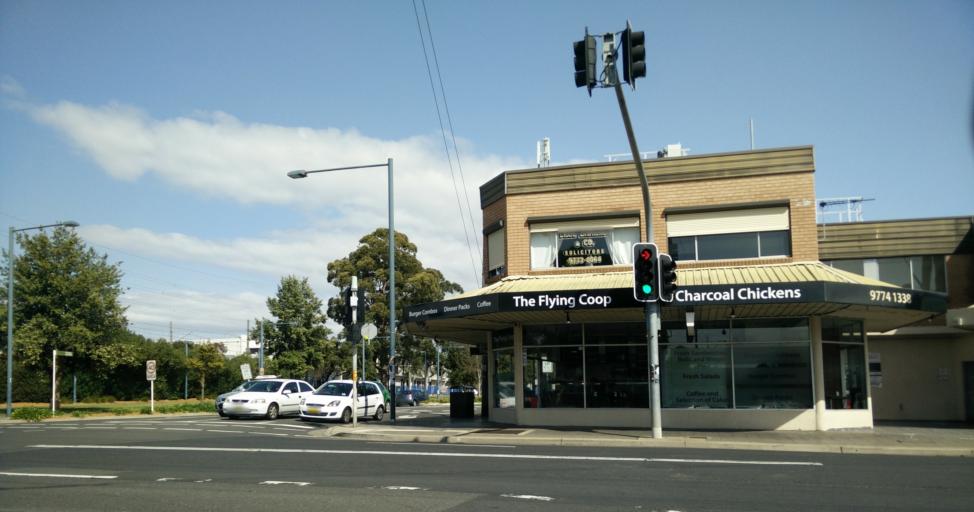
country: AU
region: New South Wales
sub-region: Bankstown
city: Revesby
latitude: -33.9518
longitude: 151.0172
